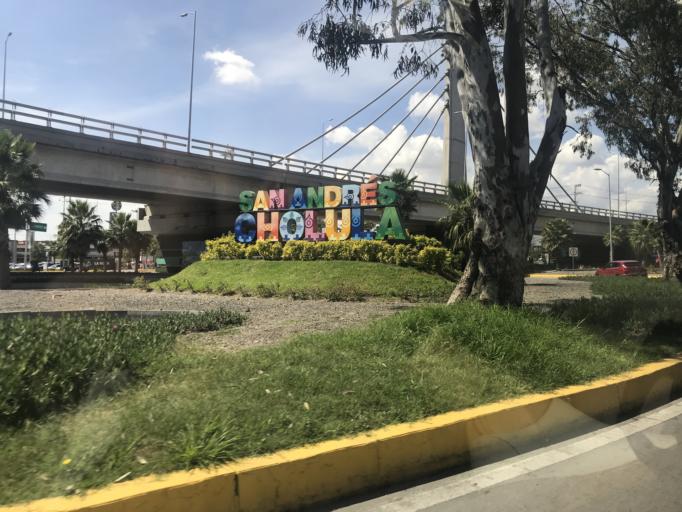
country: MX
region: Puebla
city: Cholula
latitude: 19.0602
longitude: -98.2946
